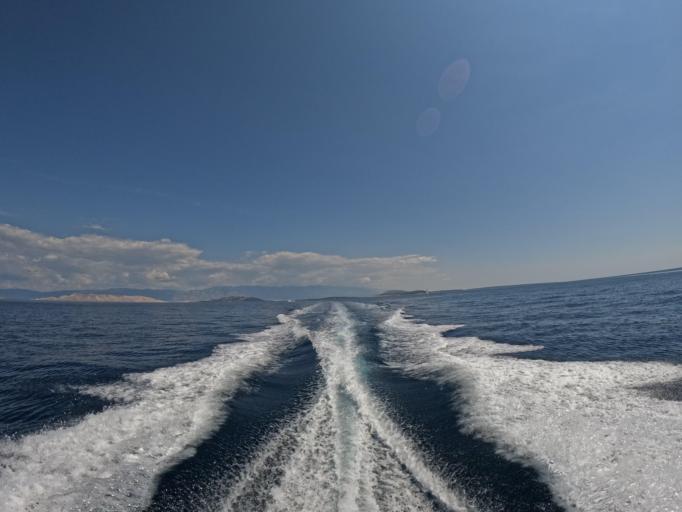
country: HR
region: Primorsko-Goranska
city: Punat
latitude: 44.8961
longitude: 14.6205
